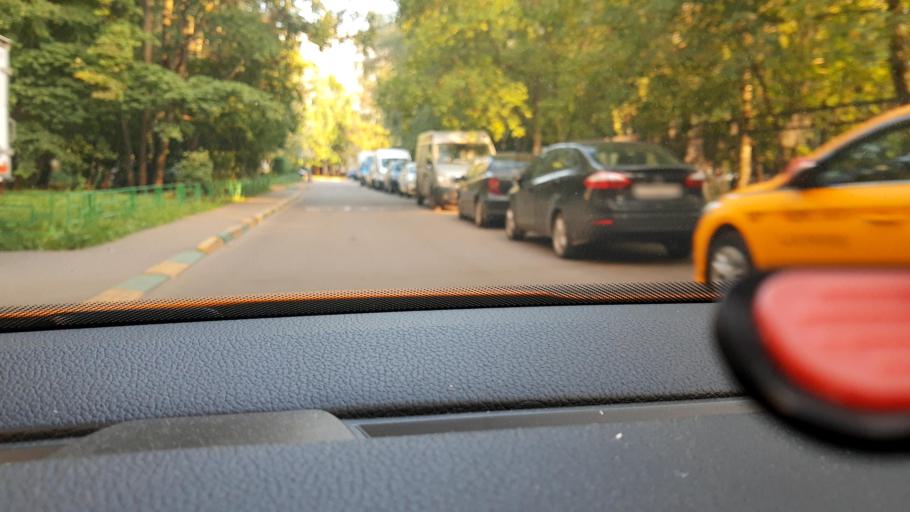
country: RU
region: Moscow
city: Khimki
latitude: 55.9004
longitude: 37.4120
